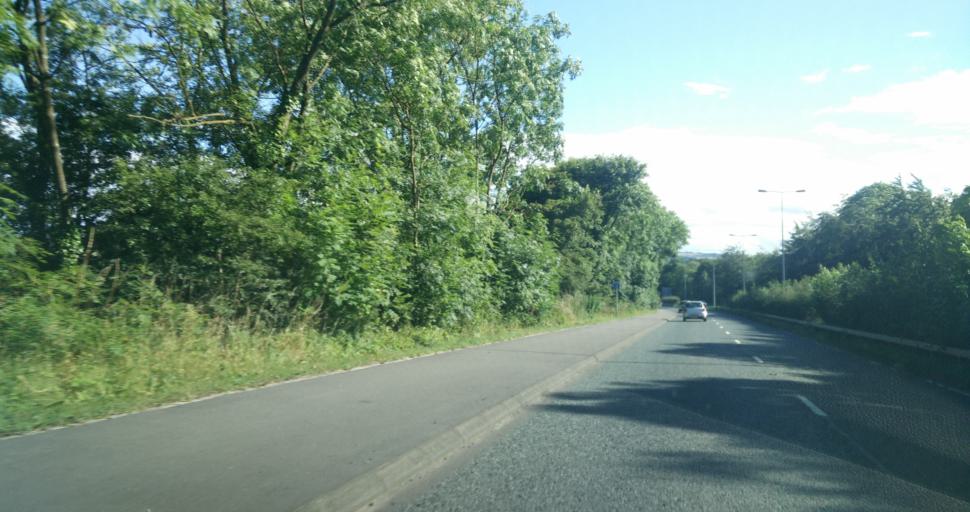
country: GB
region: England
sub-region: County Durham
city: Durham
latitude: 54.7508
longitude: -1.5905
